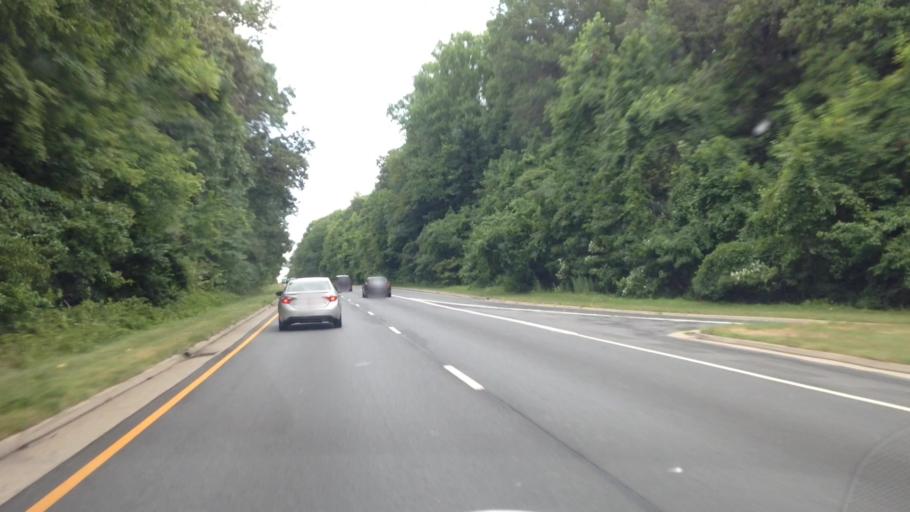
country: US
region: Maryland
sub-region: Prince George's County
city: Greenbelt
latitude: 39.0069
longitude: -76.8625
